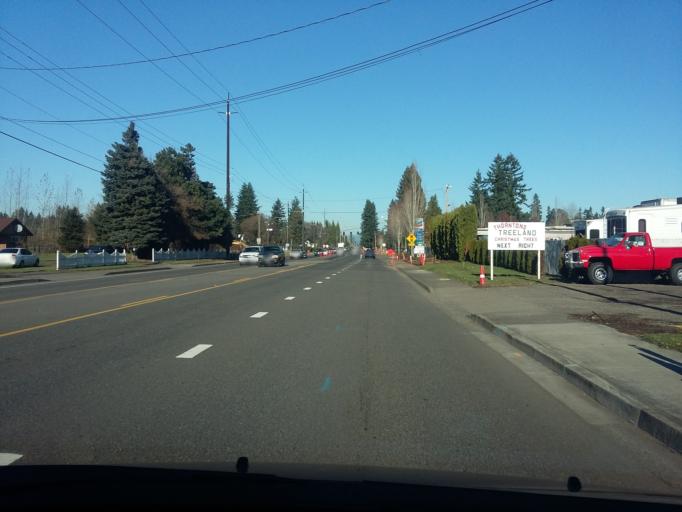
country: US
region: Washington
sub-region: Clark County
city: Barberton
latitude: 45.7060
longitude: -122.5993
